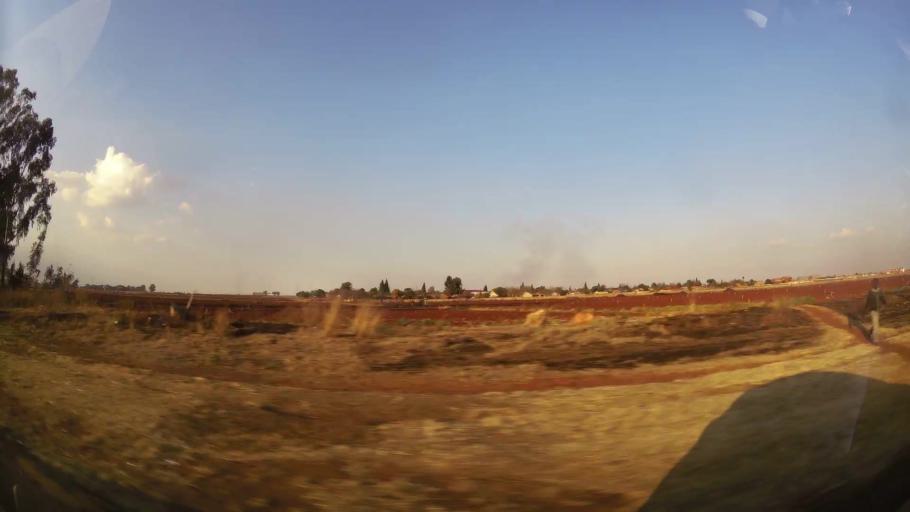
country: ZA
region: Gauteng
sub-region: Ekurhuleni Metropolitan Municipality
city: Germiston
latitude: -26.3038
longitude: 28.2323
